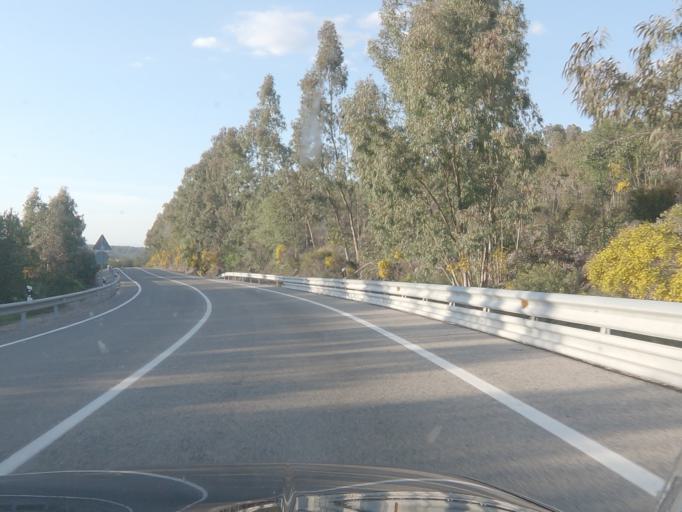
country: PT
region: Portalegre
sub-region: Portalegre
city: Sao Juliao
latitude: 39.3426
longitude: -7.2759
